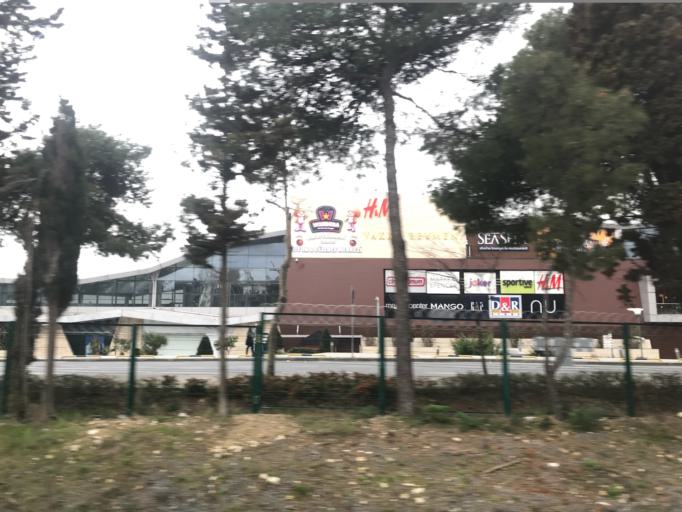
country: TR
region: Istanbul
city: Bahcelievler
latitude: 40.9665
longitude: 28.7979
